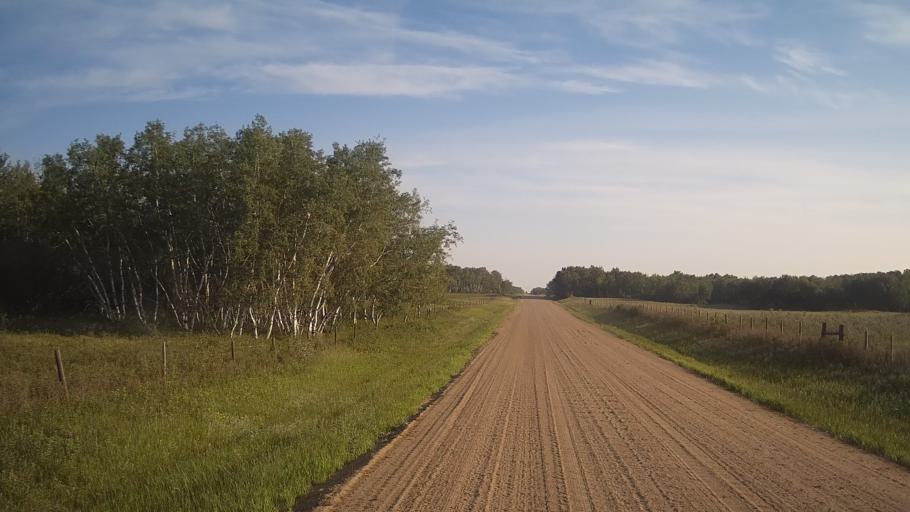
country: CA
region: Saskatchewan
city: Saskatoon
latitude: 51.8287
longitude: -106.5239
